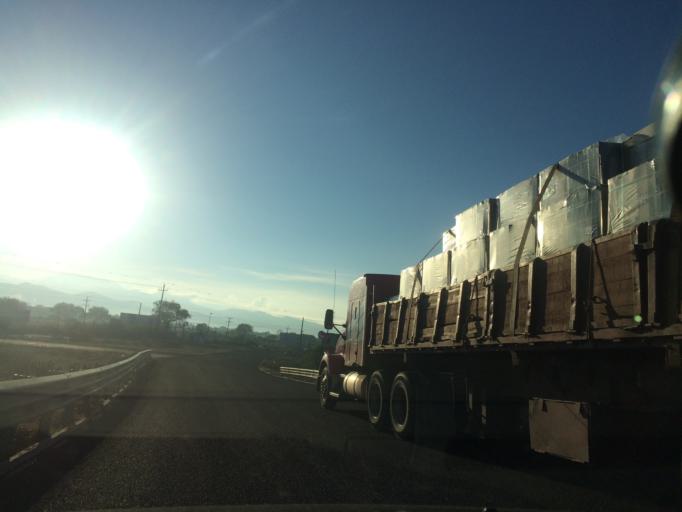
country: MX
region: Puebla
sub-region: Santiago Miahuatlan
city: San Jose Monte Chiquito
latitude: 18.4857
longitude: -97.4554
